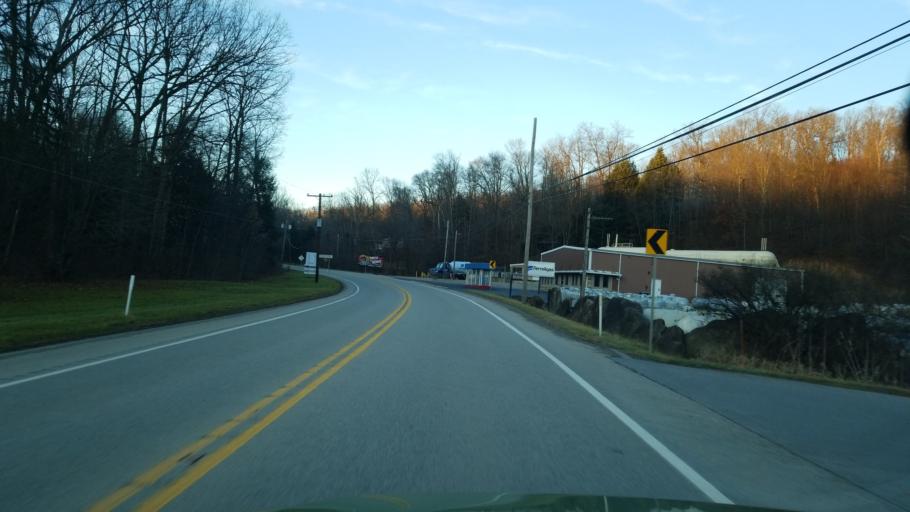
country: US
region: Pennsylvania
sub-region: Indiana County
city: Chevy Chase Heights
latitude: 40.7251
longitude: -79.1015
